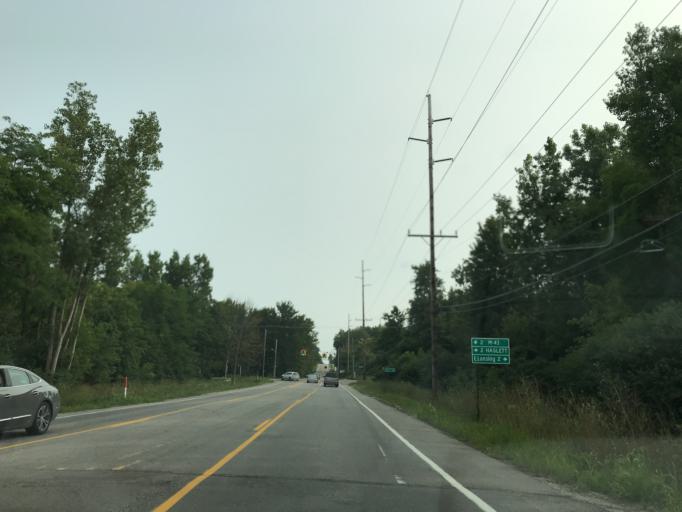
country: US
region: Michigan
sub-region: Ingham County
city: Okemos
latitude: 42.7483
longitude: -84.4475
